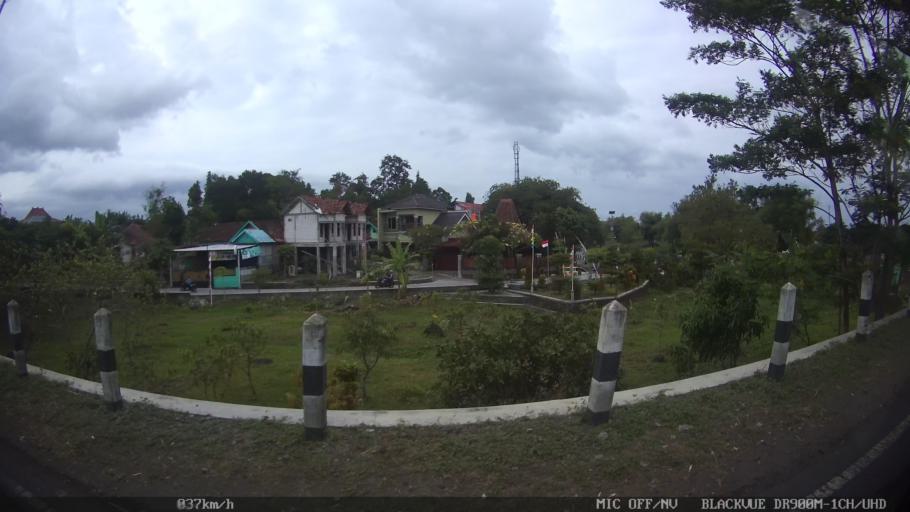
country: ID
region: Daerah Istimewa Yogyakarta
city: Depok
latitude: -7.8290
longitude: 110.4221
